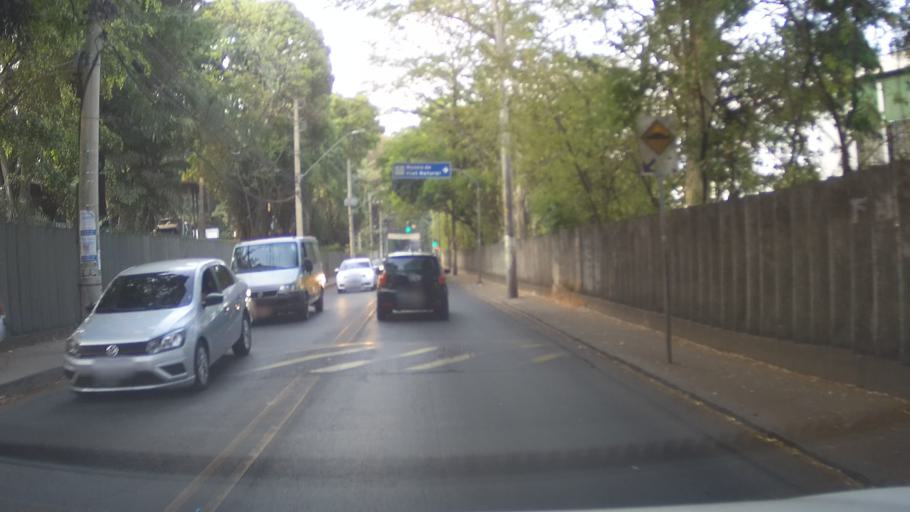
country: BR
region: Minas Gerais
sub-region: Belo Horizonte
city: Belo Horizonte
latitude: -19.8967
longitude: -43.9118
